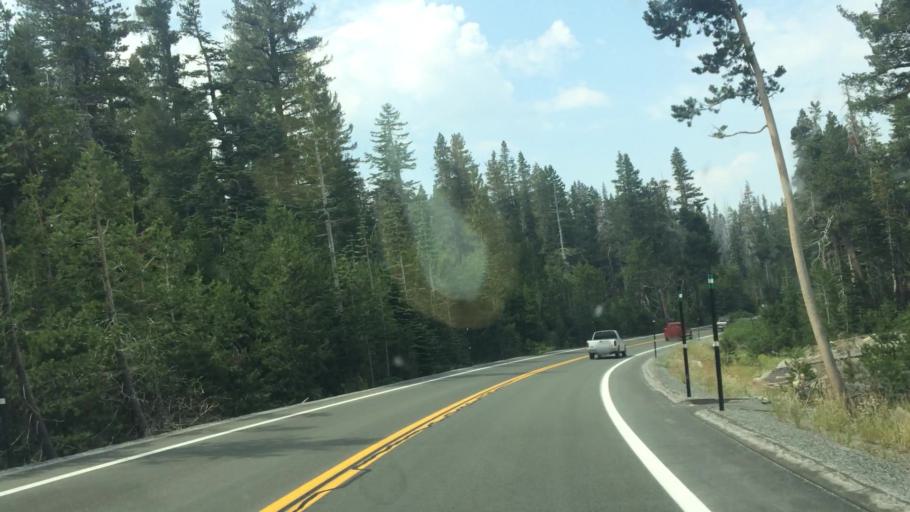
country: US
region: California
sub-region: El Dorado County
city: South Lake Tahoe
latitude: 38.6537
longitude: -120.1345
